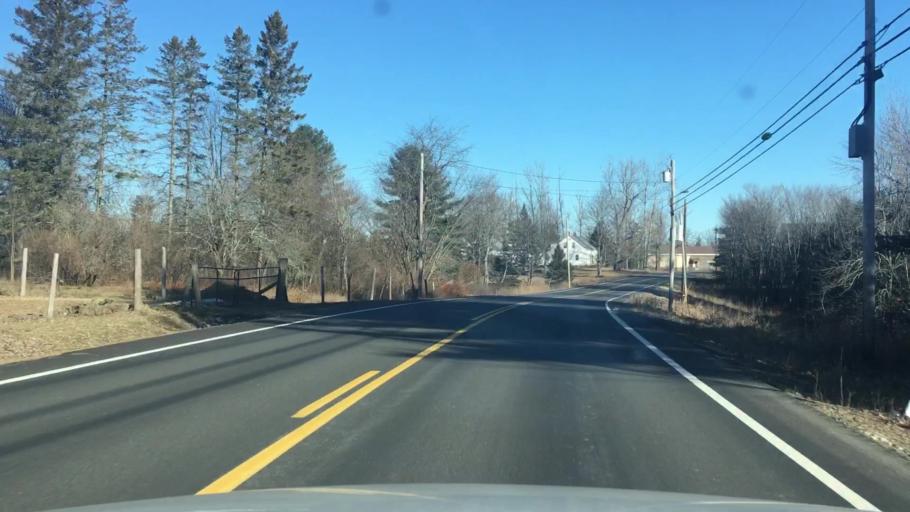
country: US
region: Maine
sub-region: Kennebec County
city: Benton
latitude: 44.6025
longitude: -69.5395
